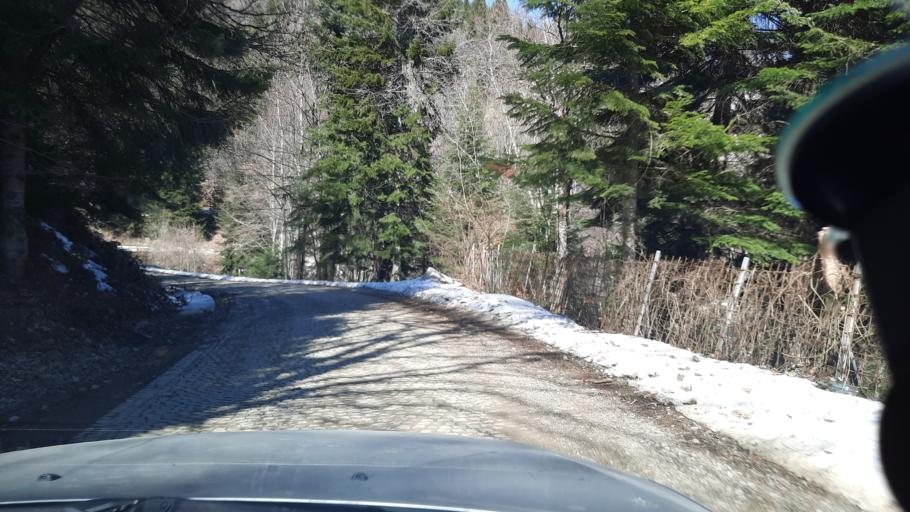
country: MK
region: Gostivar
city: Vrutok
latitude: 41.7029
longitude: 20.7577
